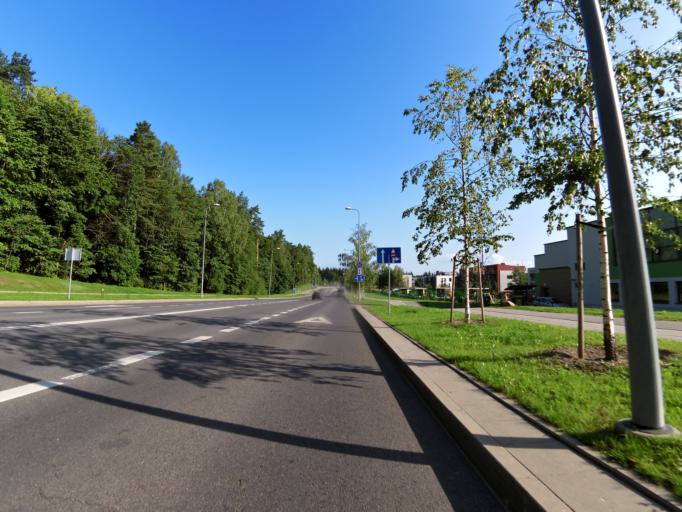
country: LT
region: Vilnius County
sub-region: Vilnius
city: Fabijoniskes
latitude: 54.7615
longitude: 25.2820
